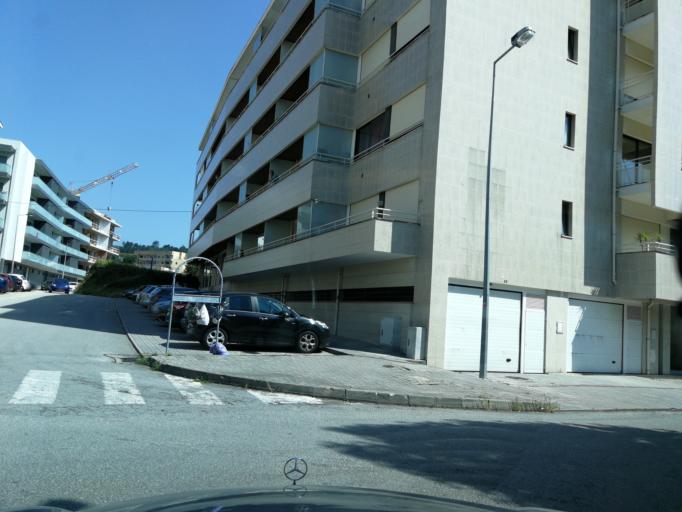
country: PT
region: Braga
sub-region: Braga
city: Adaufe
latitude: 41.5634
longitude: -8.3907
